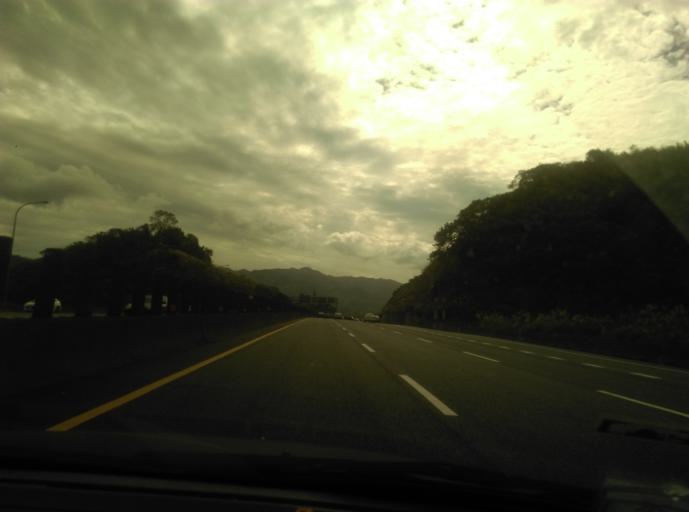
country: TW
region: Taiwan
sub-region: Keelung
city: Keelung
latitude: 25.0920
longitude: 121.6962
